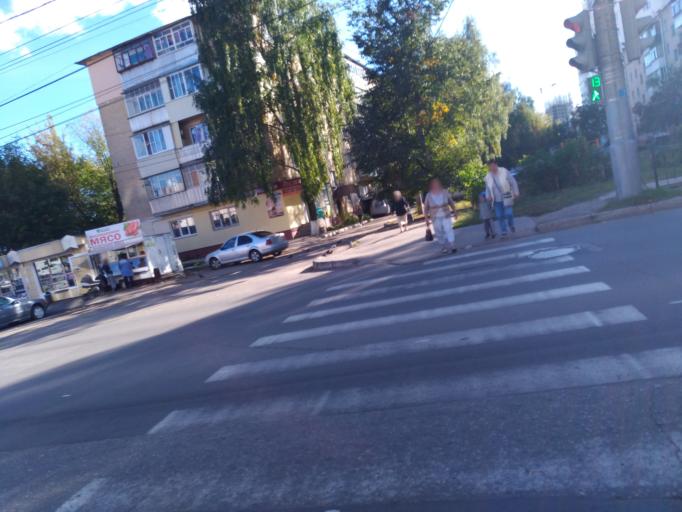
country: RU
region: Kaluga
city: Kaluga
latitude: 54.5308
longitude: 36.2673
